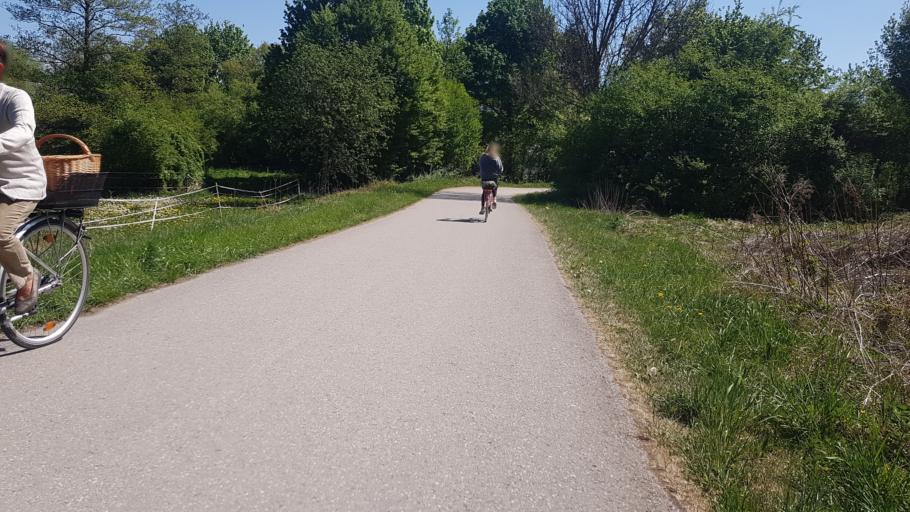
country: DE
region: Bavaria
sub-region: Upper Bavaria
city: Unterfoehring
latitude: 48.1766
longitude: 11.6521
